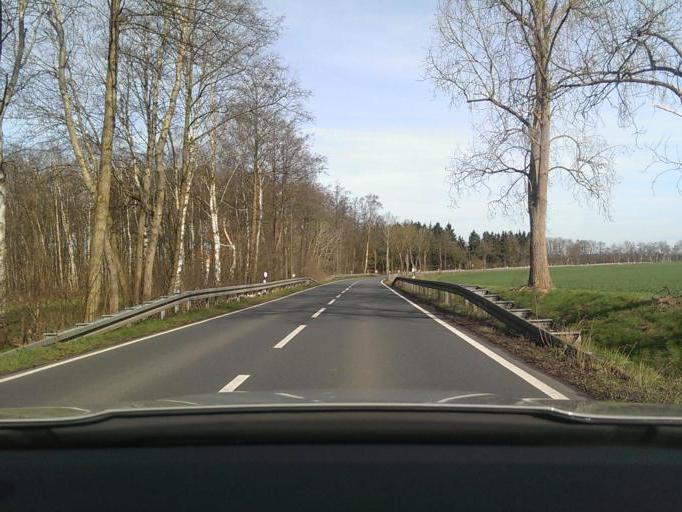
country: DE
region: Lower Saxony
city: Garbsen-Mitte
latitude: 52.5292
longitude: 9.6163
